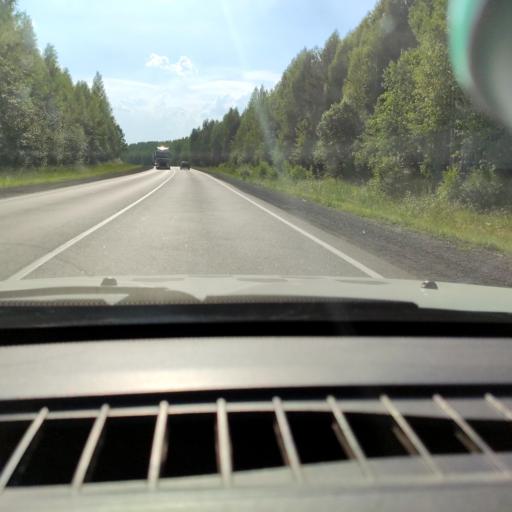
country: RU
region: Perm
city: Ocher
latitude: 57.7524
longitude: 54.4141
